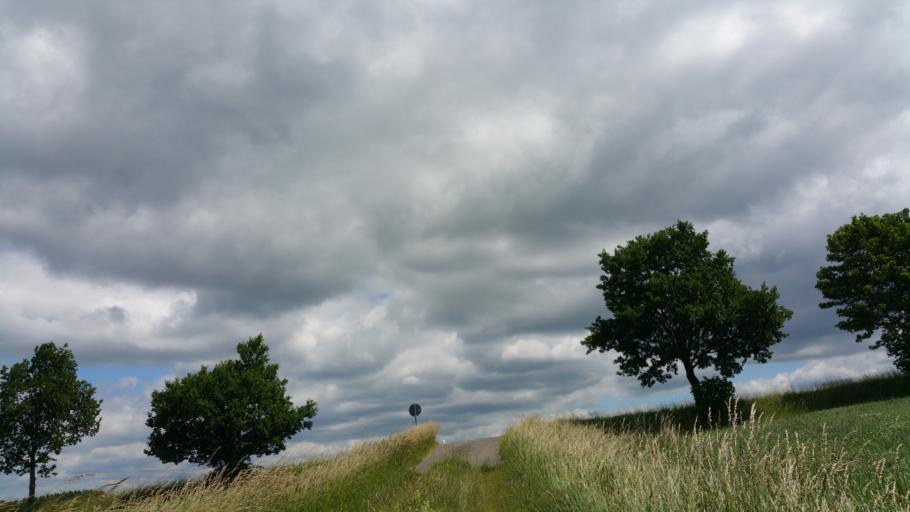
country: DE
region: Bavaria
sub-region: Upper Franconia
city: Schwarzenbach an der Saale
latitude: 50.2097
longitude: 11.9318
